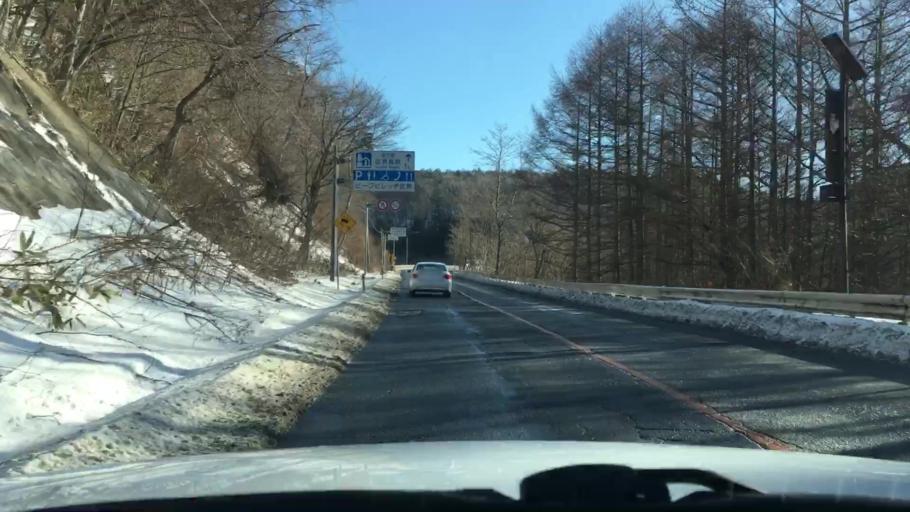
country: JP
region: Iwate
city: Morioka-shi
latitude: 39.6563
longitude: 141.3423
